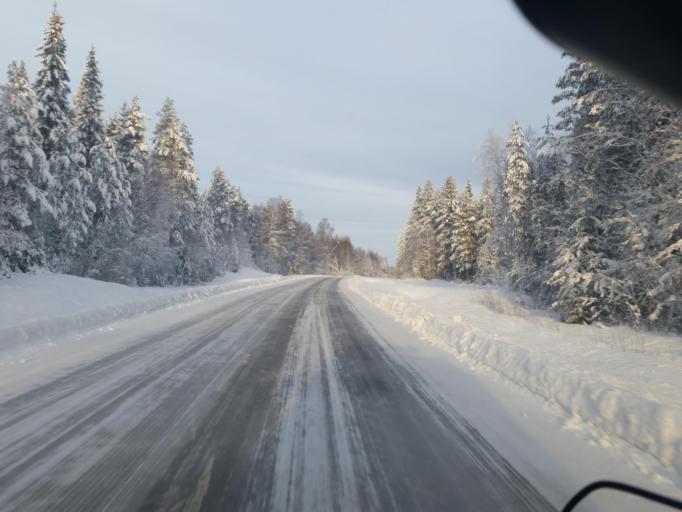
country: SE
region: Norrbotten
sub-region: Pitea Kommun
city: Norrfjarden
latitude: 65.4856
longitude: 21.4699
